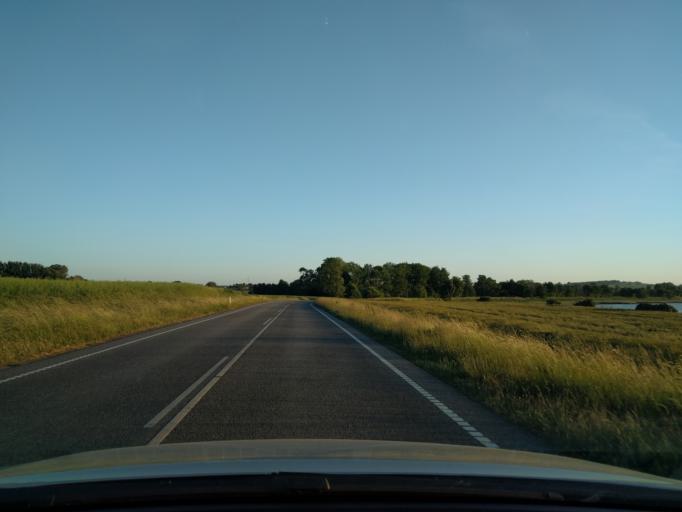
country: DK
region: South Denmark
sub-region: Kerteminde Kommune
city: Kerteminde
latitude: 55.4796
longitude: 10.6158
